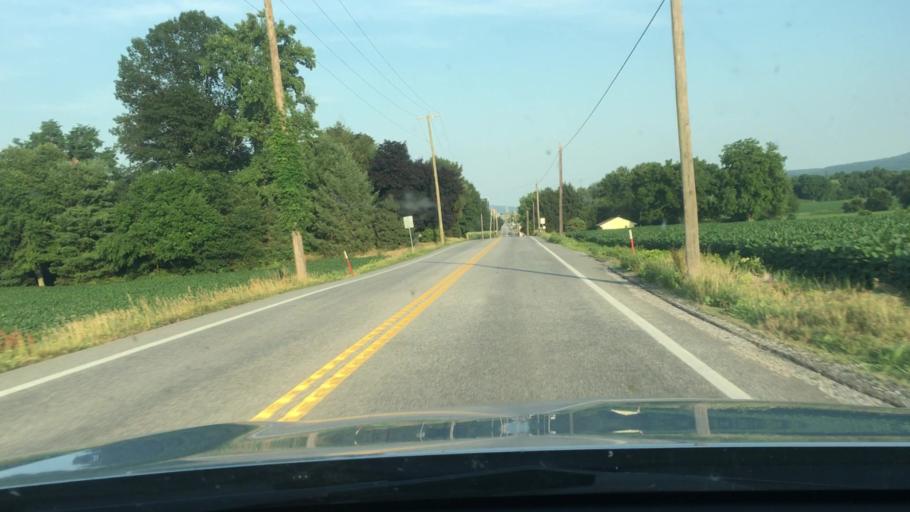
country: US
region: Pennsylvania
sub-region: Cumberland County
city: Boiling Springs
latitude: 40.1647
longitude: -77.1035
